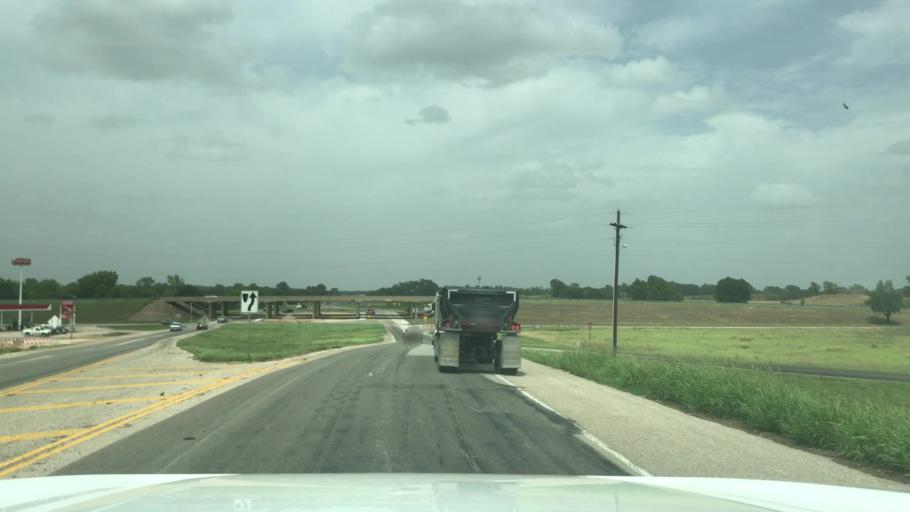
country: US
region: Texas
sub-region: McLennan County
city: Bellmead
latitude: 31.5444
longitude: -97.0698
